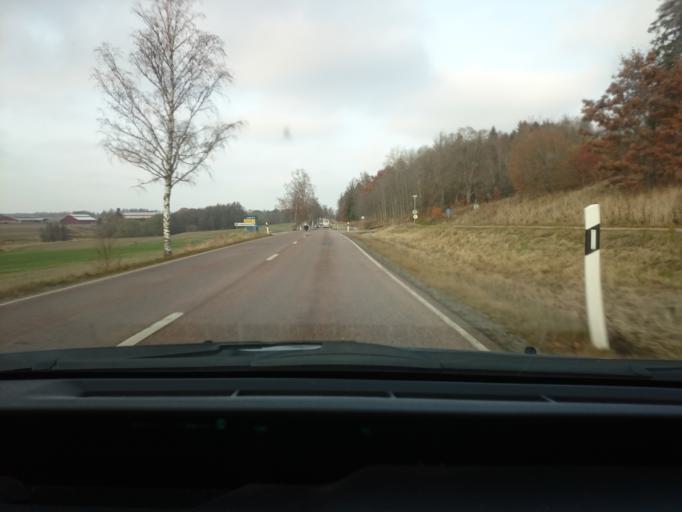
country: SE
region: Vaestmanland
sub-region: Vasteras
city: Skultuna
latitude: 59.6683
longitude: 16.4777
